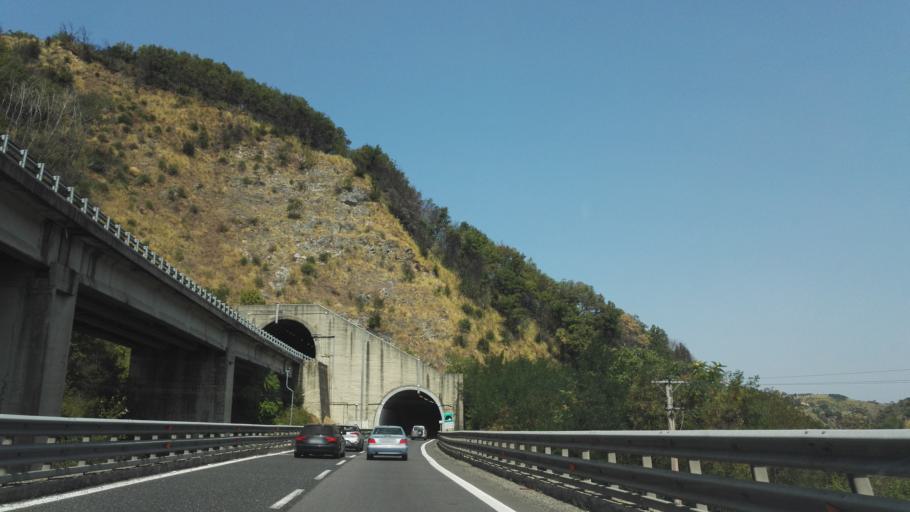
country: IT
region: Calabria
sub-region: Provincia di Cosenza
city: Dipignano
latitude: 39.2593
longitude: 16.2546
